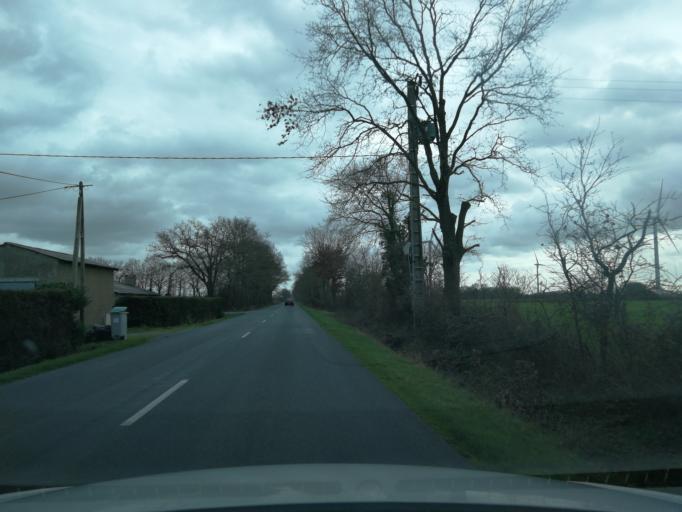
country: FR
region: Pays de la Loire
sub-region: Departement de la Loire-Atlantique
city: Montbert
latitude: 47.0143
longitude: -1.4822
